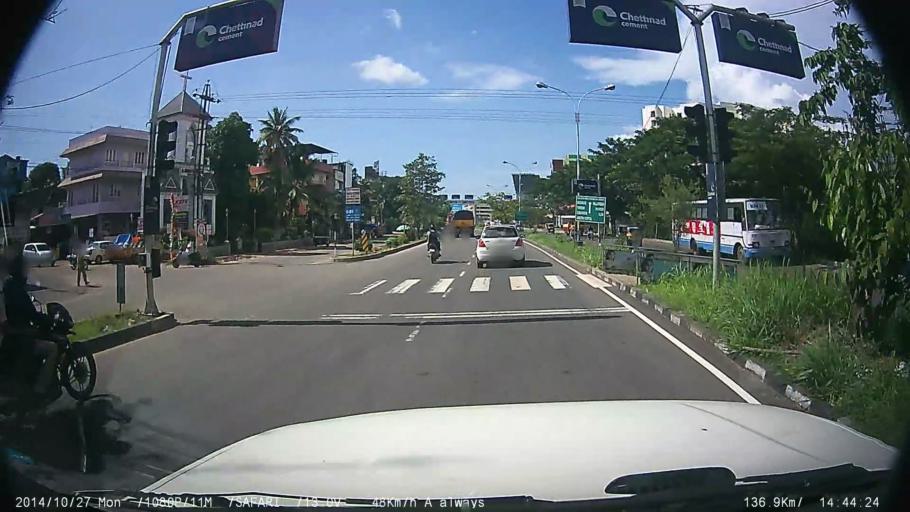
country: IN
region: Kerala
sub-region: Ernakulam
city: Elur
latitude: 10.0205
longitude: 76.3104
